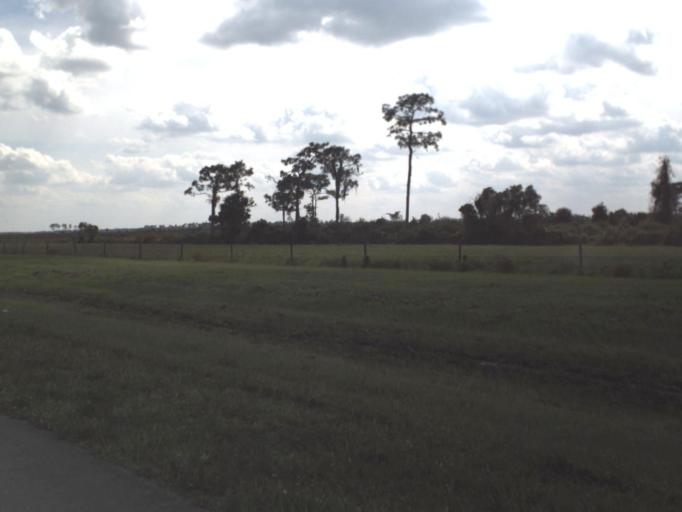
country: US
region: Florida
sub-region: Indian River County
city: Fellsmere
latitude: 27.6380
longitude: -80.8722
